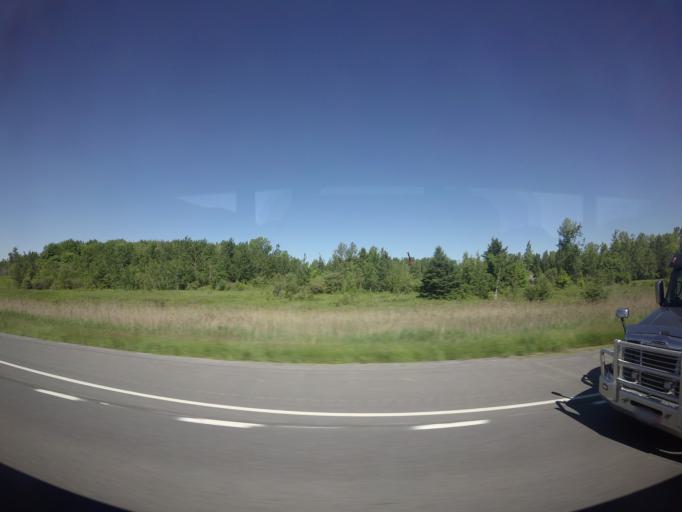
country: CA
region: Quebec
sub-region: Mauricie
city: Saint-Germain-de-Grantham
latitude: 45.7905
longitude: -72.6592
